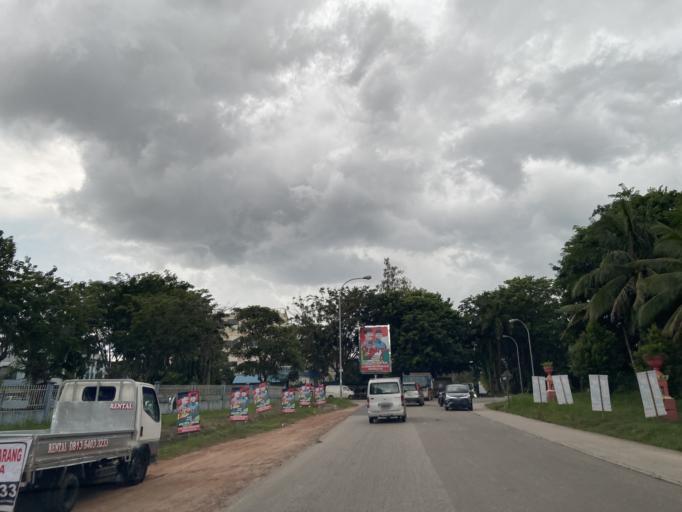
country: SG
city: Singapore
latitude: 1.1106
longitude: 104.0430
